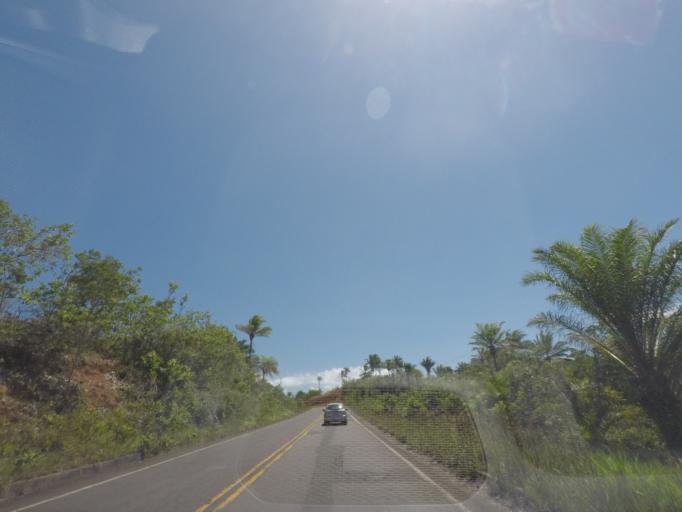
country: BR
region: Bahia
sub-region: Valenca
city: Valenca
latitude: -13.3086
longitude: -39.0345
